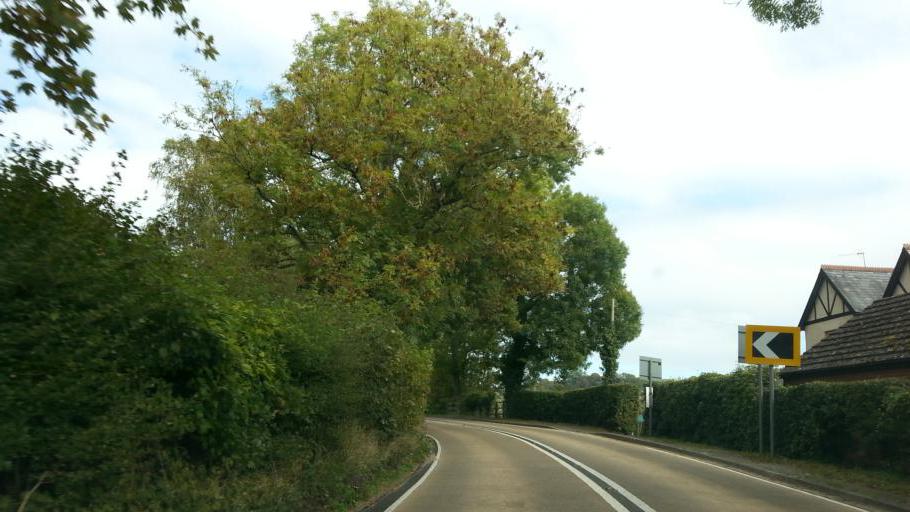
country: GB
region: England
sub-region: Gloucestershire
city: Stroud
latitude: 51.7700
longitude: -2.2157
